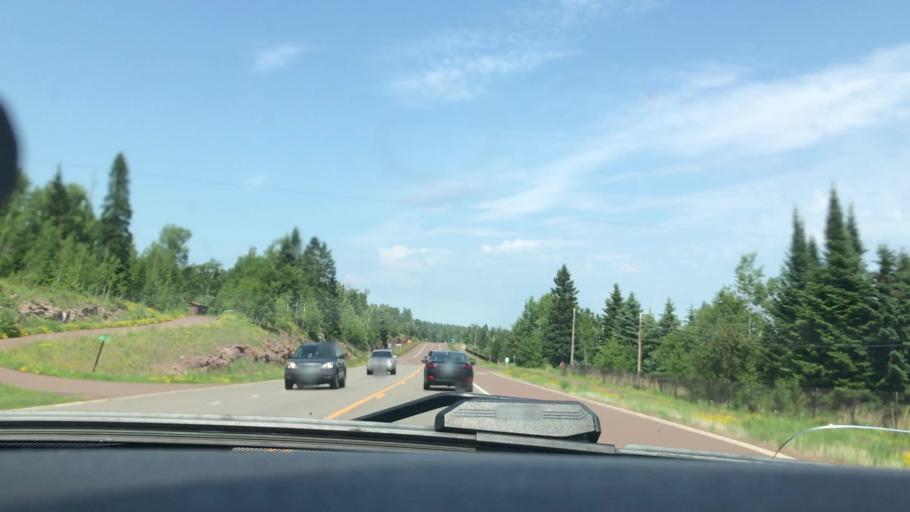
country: US
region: Minnesota
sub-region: Cook County
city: Grand Marais
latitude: 47.5999
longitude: -90.7879
